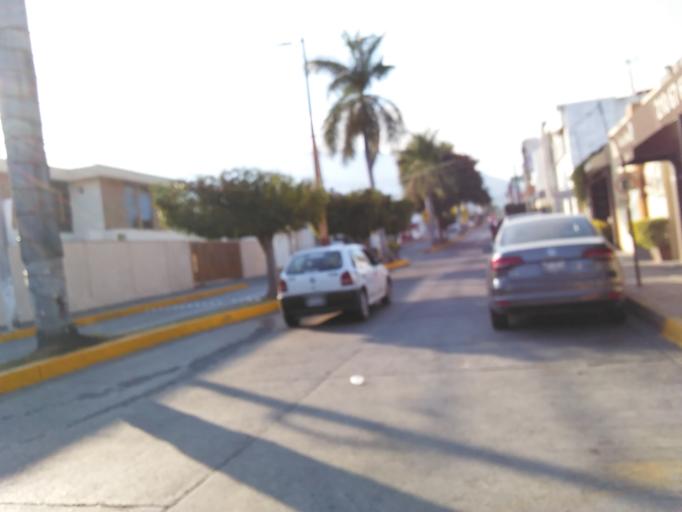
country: MX
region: Nayarit
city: Tepic
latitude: 21.5002
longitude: -104.9008
